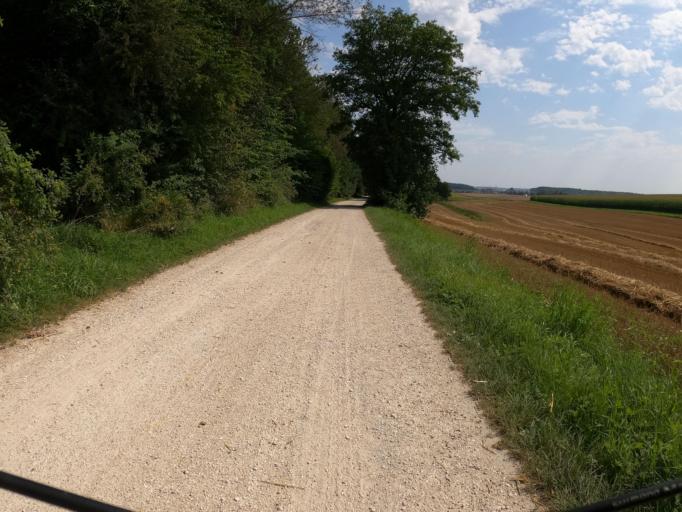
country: DE
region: Bavaria
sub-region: Swabia
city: Rieden an der Kotz
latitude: 48.3675
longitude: 10.2361
